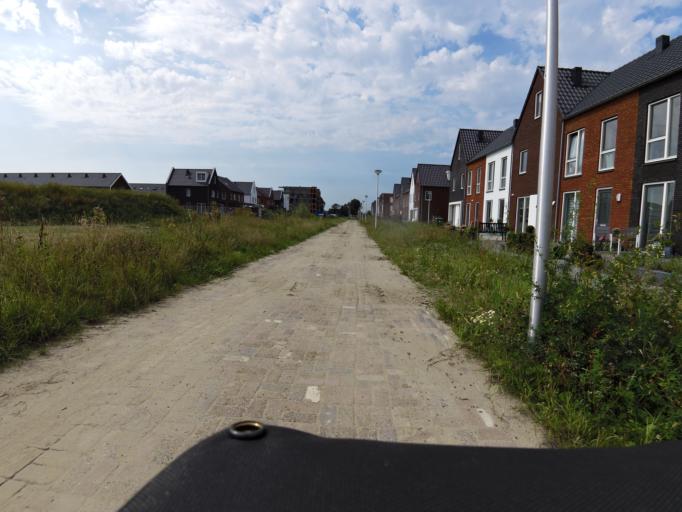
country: NL
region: South Holland
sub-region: Gemeente Oud-Beijerland
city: Oud-Beijerland
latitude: 51.8131
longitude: 4.4325
